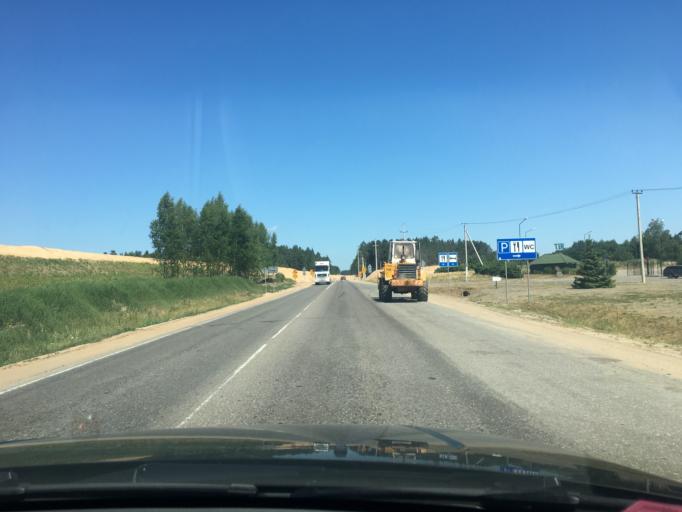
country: BY
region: Grodnenskaya
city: Iwye
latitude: 53.8832
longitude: 25.7403
